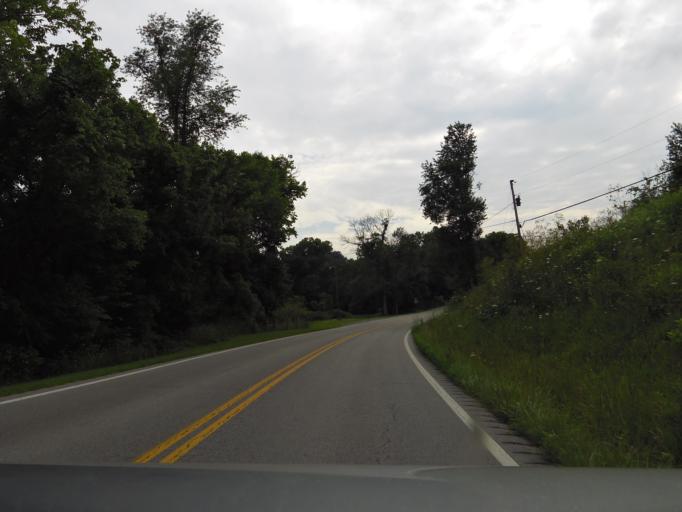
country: US
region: Kentucky
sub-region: Robertson County
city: Mount Olivet
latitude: 38.4927
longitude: -84.1099
